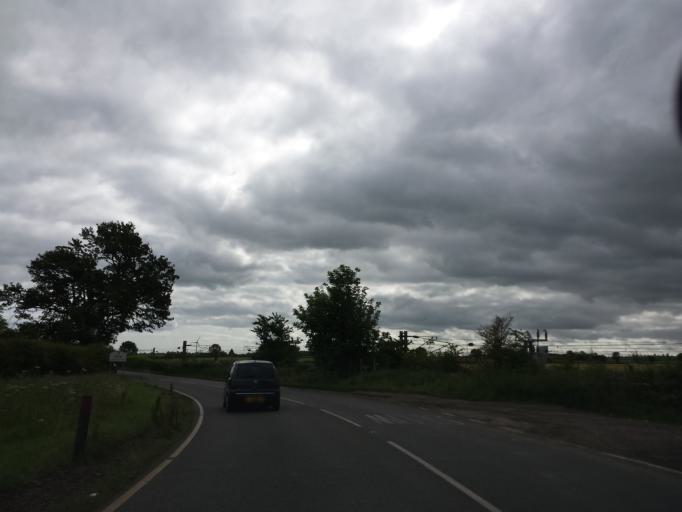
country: GB
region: Scotland
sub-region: East Lothian
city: Haddington
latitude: 56.0046
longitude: -2.7910
